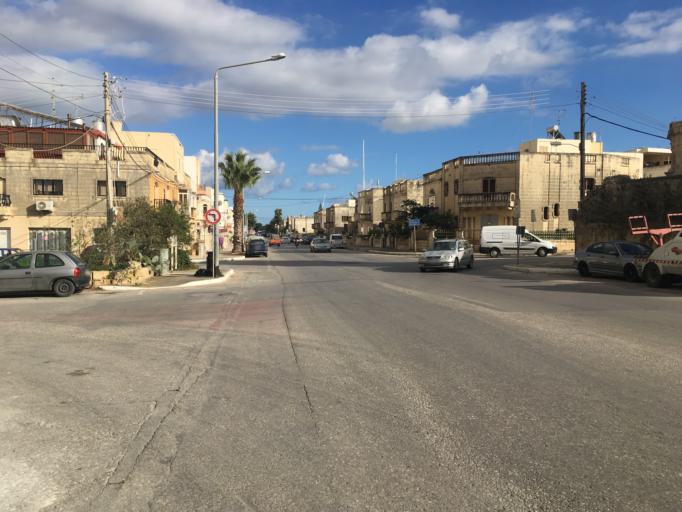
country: MT
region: Il-Mosta
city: Mosta
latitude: 35.9056
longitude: 14.4255
